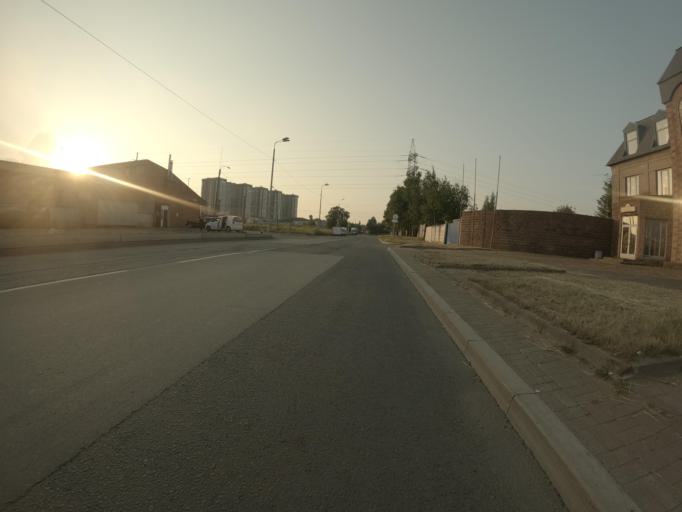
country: RU
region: St.-Petersburg
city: Krasnogvargeisky
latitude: 59.9737
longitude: 30.4407
